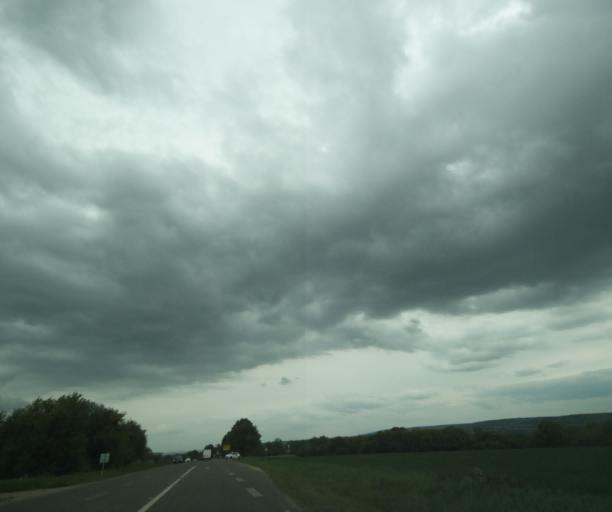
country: FR
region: Ile-de-France
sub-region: Departement des Yvelines
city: Flins-sur-Seine
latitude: 48.9589
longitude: 1.8852
